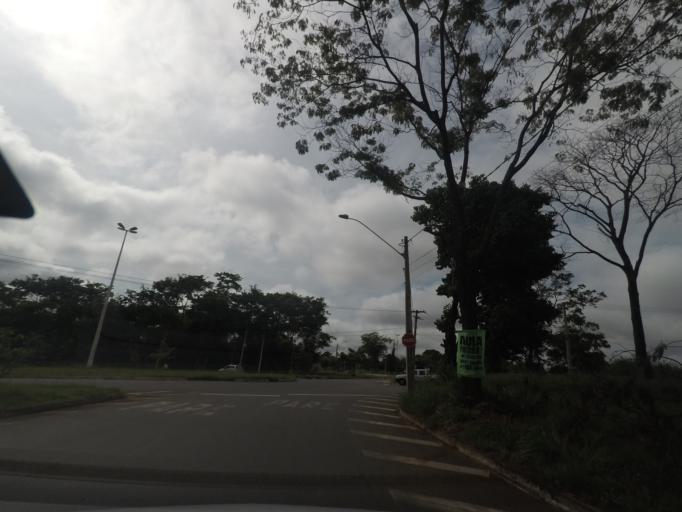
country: BR
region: Goias
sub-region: Goiania
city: Goiania
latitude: -16.7448
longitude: -49.3109
